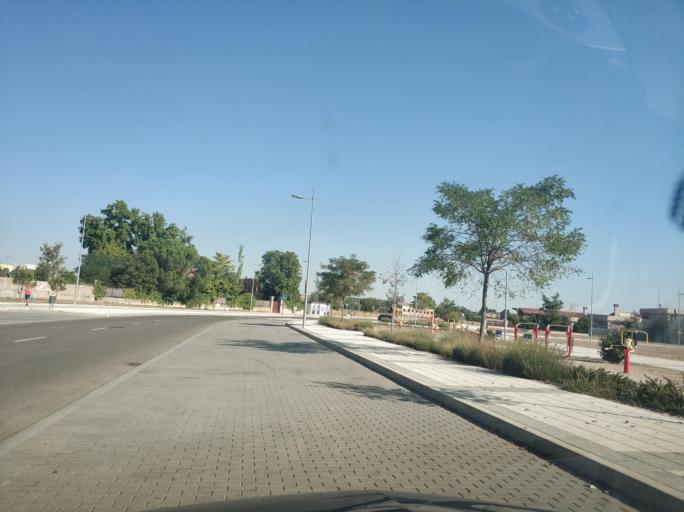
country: ES
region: Castille and Leon
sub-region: Provincia de Burgos
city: Aranda de Duero
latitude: 41.6690
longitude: -3.6961
